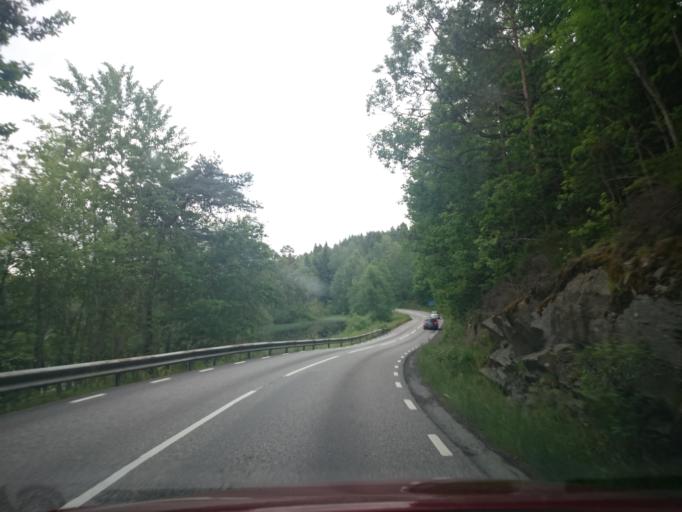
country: SE
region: Vaestra Goetaland
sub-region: Lerums Kommun
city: Stenkullen
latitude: 57.7345
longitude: 12.3452
